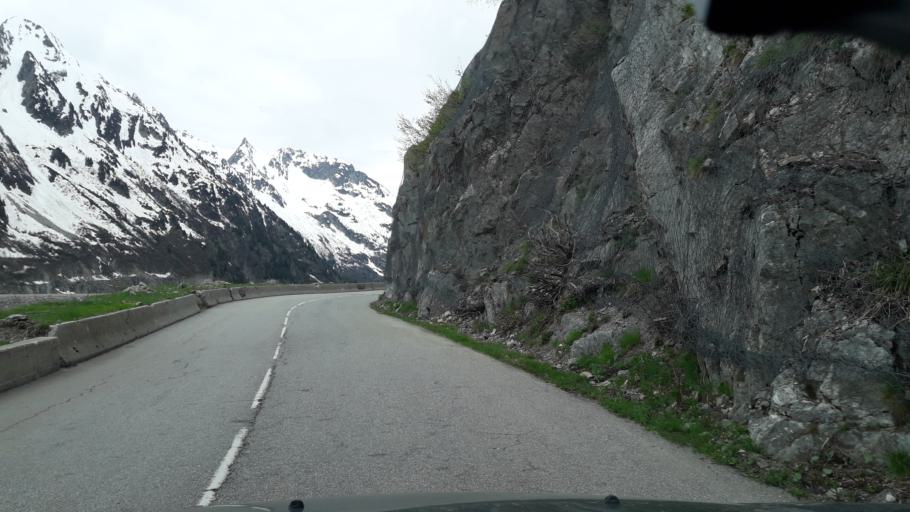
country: FR
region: Rhone-Alpes
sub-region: Departement de l'Isere
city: Huez
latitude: 45.2087
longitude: 6.1189
